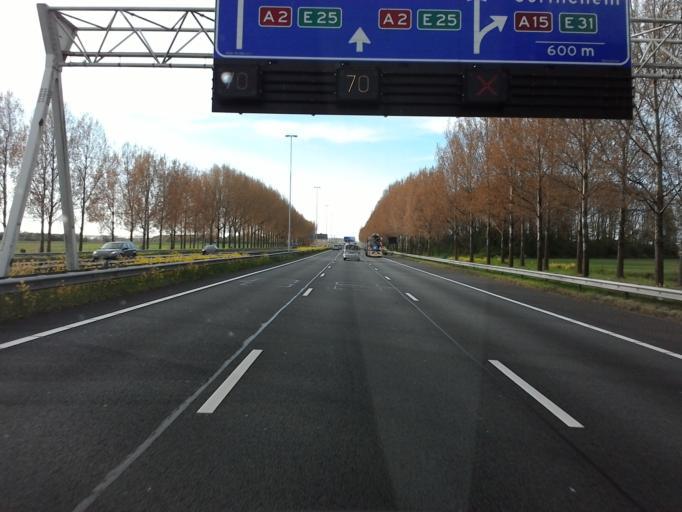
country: NL
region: Gelderland
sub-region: Gemeente Zaltbommel
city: Zaltbommel
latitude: 51.8419
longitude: 5.2432
